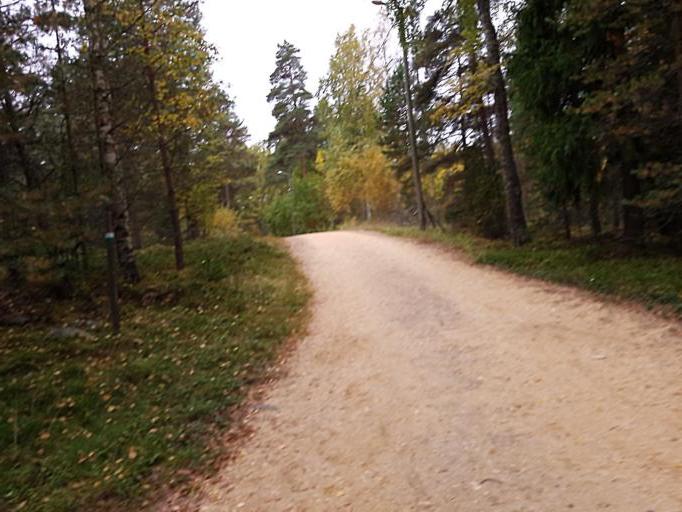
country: FI
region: Uusimaa
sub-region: Helsinki
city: Helsinki
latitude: 60.2651
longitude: 24.9104
